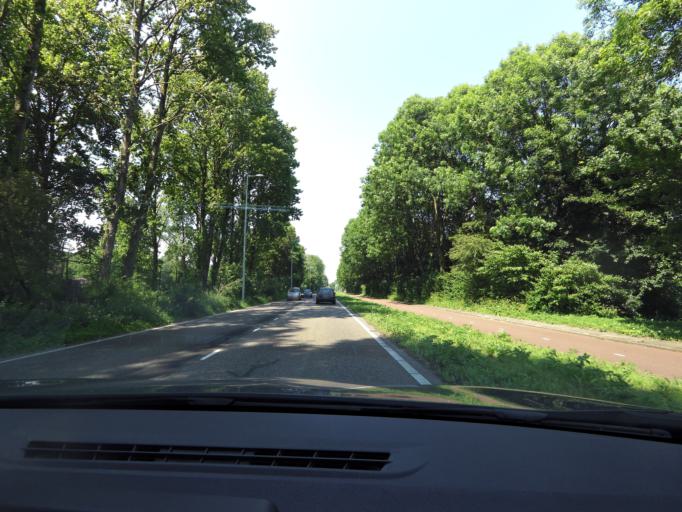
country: NL
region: South Holland
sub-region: Gemeente Rotterdam
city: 's-Gravenland
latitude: 51.9339
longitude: 4.5321
